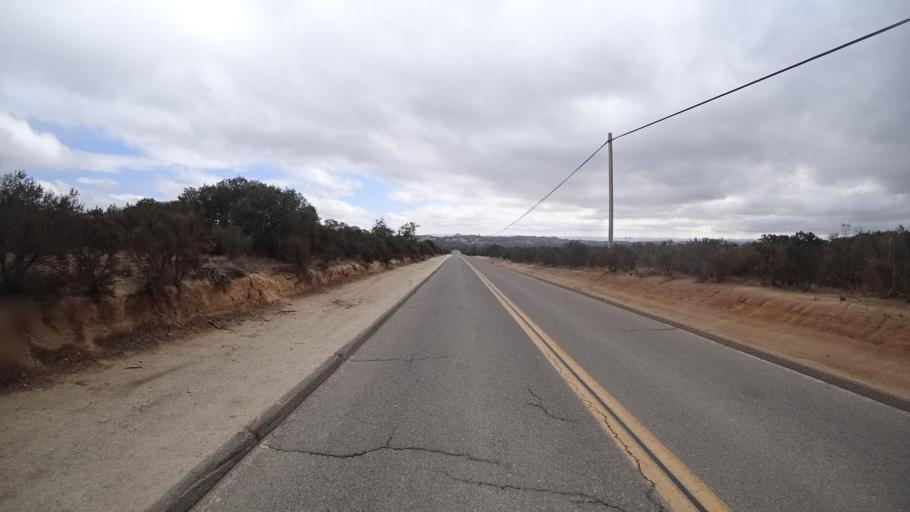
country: US
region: California
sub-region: San Diego County
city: Campo
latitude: 32.6095
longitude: -116.3297
